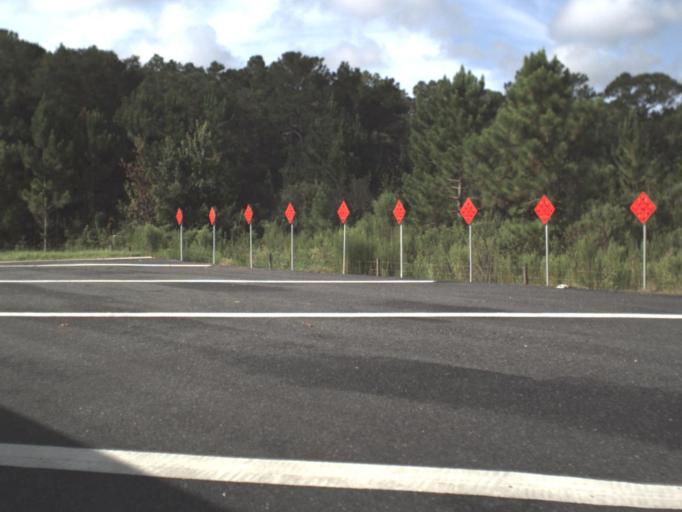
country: US
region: Florida
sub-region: Pasco County
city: Land O' Lakes
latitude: 28.2889
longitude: -82.4886
